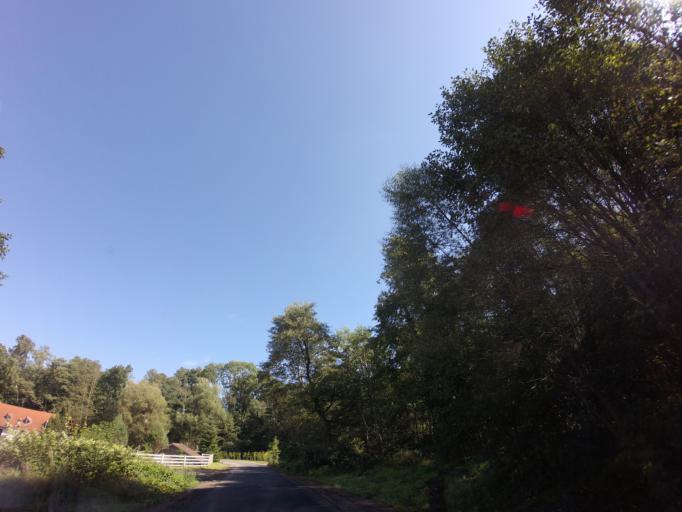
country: PL
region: West Pomeranian Voivodeship
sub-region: Powiat choszczenski
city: Choszczno
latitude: 53.1841
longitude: 15.5012
